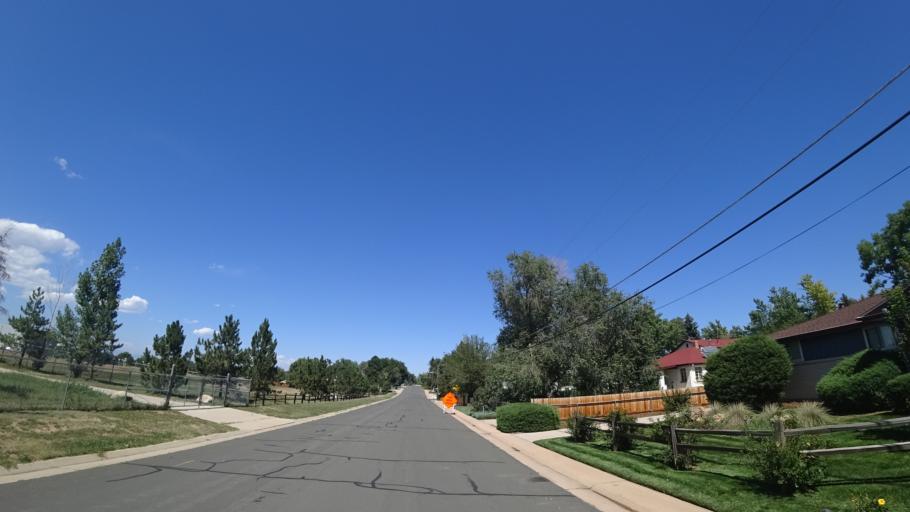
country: US
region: Colorado
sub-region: Arapahoe County
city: Littleton
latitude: 39.6060
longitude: -104.9846
